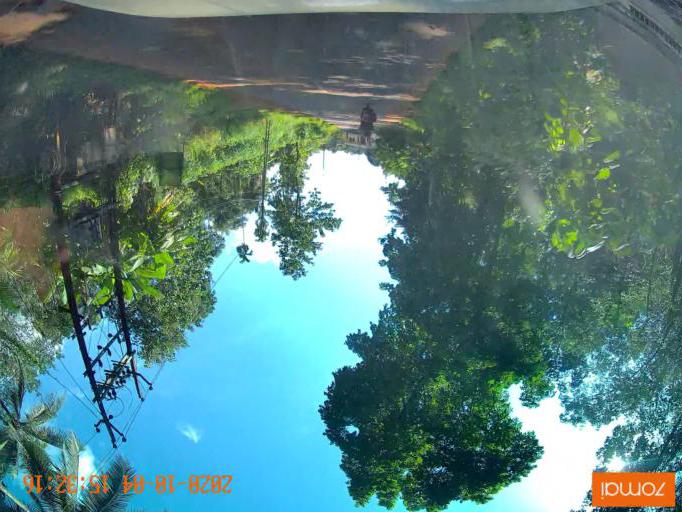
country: IN
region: Kerala
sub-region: Kottayam
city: Palackattumala
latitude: 9.7342
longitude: 76.6353
